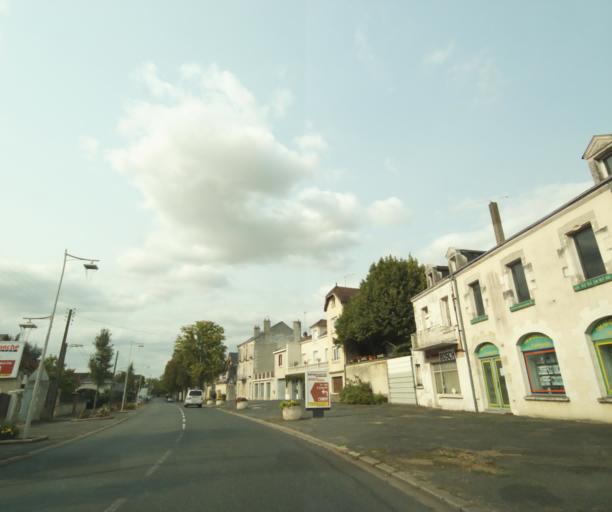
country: FR
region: Centre
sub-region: Departement de l'Indre
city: Chatillon-sur-Indre
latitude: 46.9850
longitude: 1.1733
